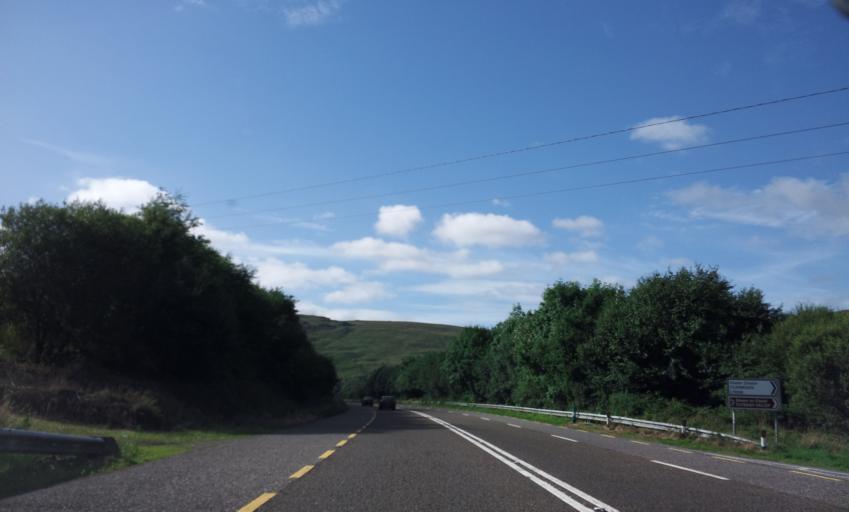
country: IE
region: Munster
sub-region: County Cork
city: Millstreet
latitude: 51.9855
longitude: -9.2833
